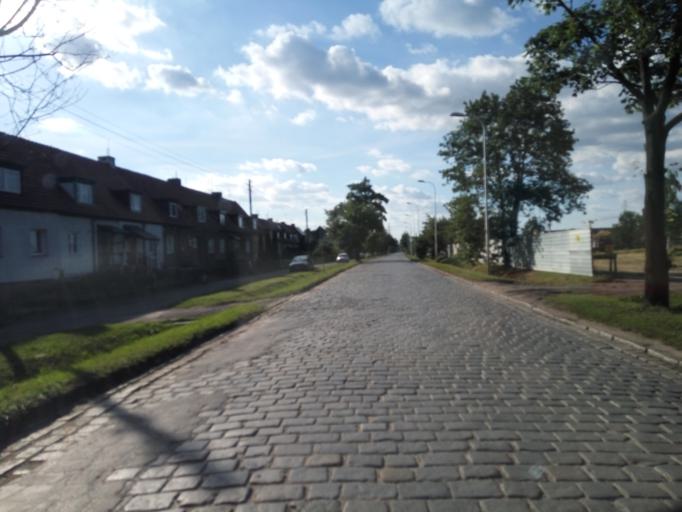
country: PL
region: Lower Silesian Voivodeship
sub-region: Powiat trzebnicki
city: Psary
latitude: 51.1502
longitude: 16.9436
